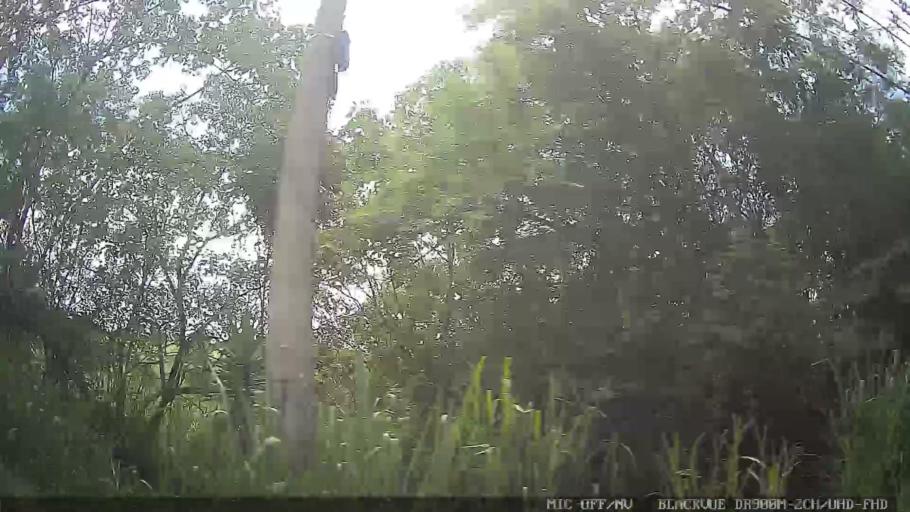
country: BR
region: Sao Paulo
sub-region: Santa Isabel
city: Santa Isabel
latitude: -23.4129
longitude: -46.2064
